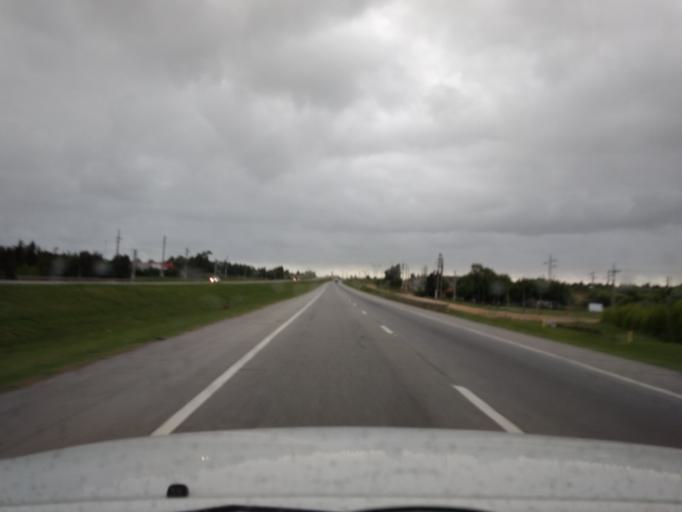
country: UY
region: Canelones
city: Las Piedras
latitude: -34.7100
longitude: -56.2426
